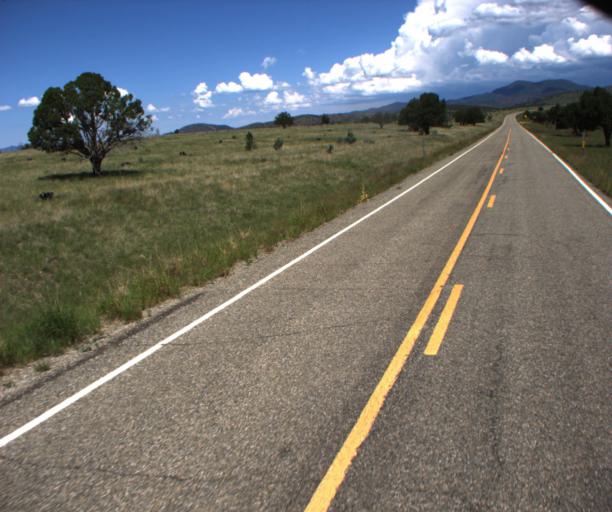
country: US
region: Arizona
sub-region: Greenlee County
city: Morenci
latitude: 33.3067
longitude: -109.3500
